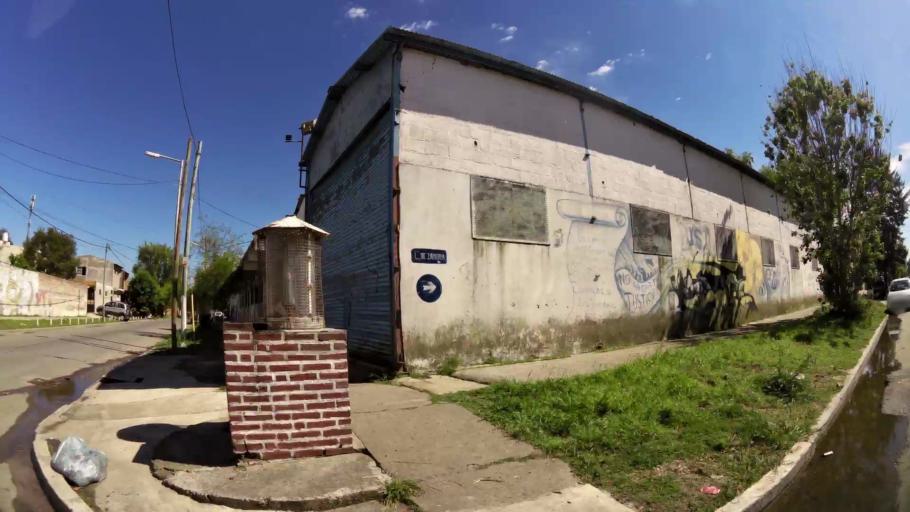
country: AR
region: Buenos Aires
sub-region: Partido de Avellaneda
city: Avellaneda
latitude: -34.6878
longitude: -58.3084
